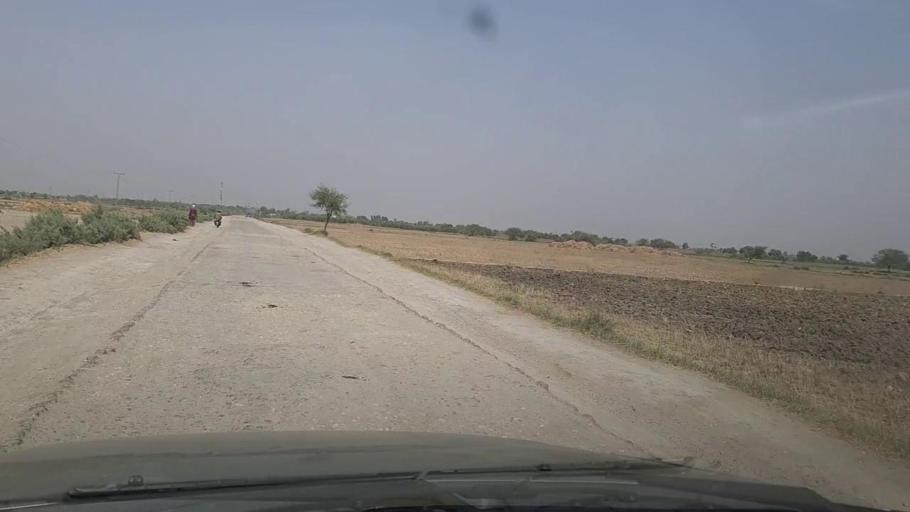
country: PK
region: Balochistan
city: Sohbatpur
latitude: 28.4199
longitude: 68.6816
